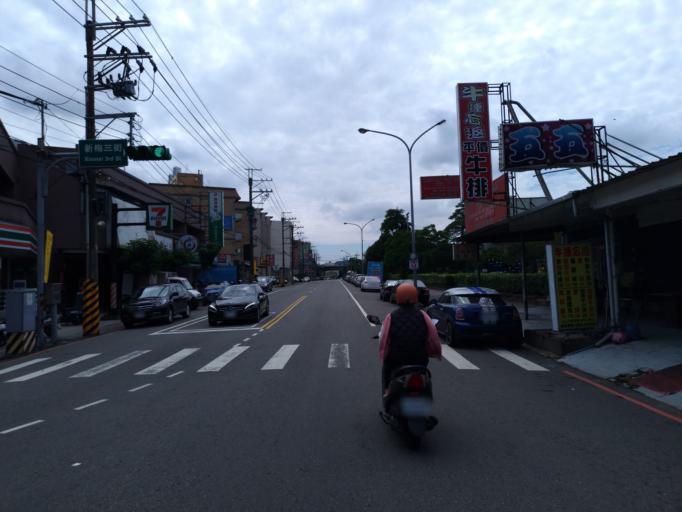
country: TW
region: Taiwan
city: Daxi
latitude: 24.9171
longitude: 121.1451
